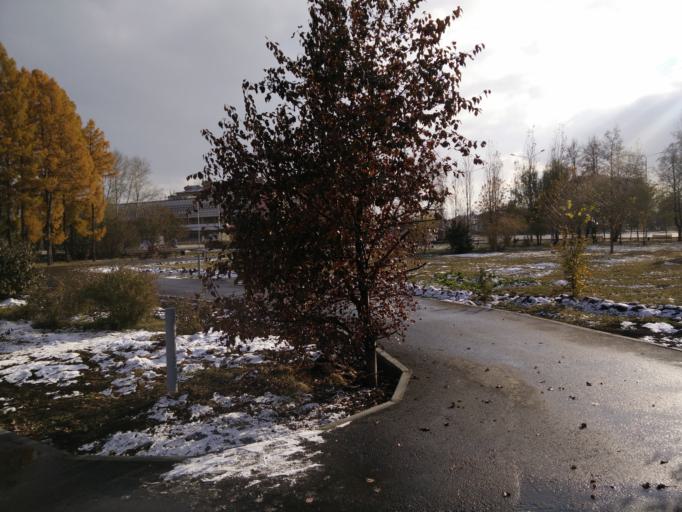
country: RU
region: Novosibirsk
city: Berdsk
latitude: 54.7577
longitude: 83.1049
